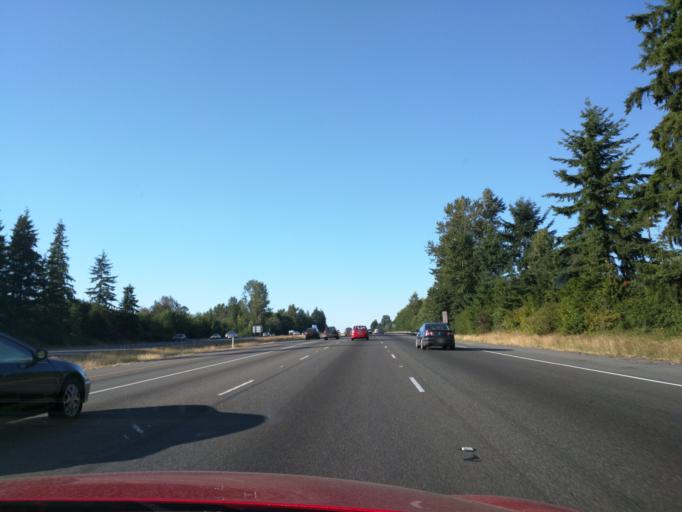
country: US
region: Washington
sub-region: Snohomish County
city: Martha Lake
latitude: 47.8565
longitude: -122.2525
